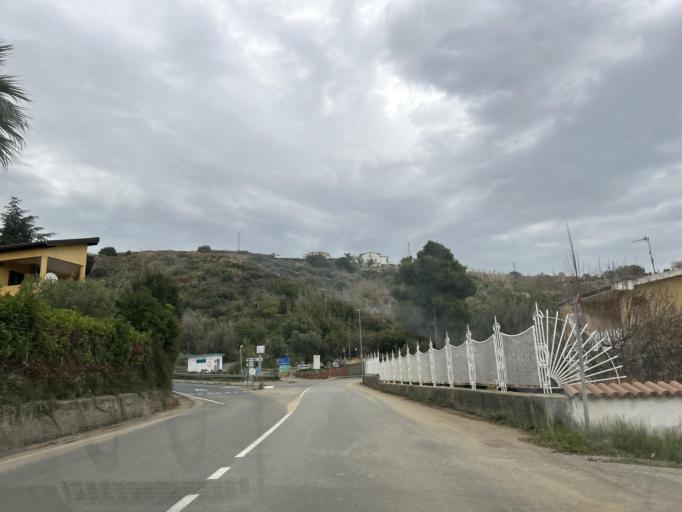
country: IT
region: Calabria
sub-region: Provincia di Catanzaro
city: Montepaone Lido
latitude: 38.7427
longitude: 16.5520
